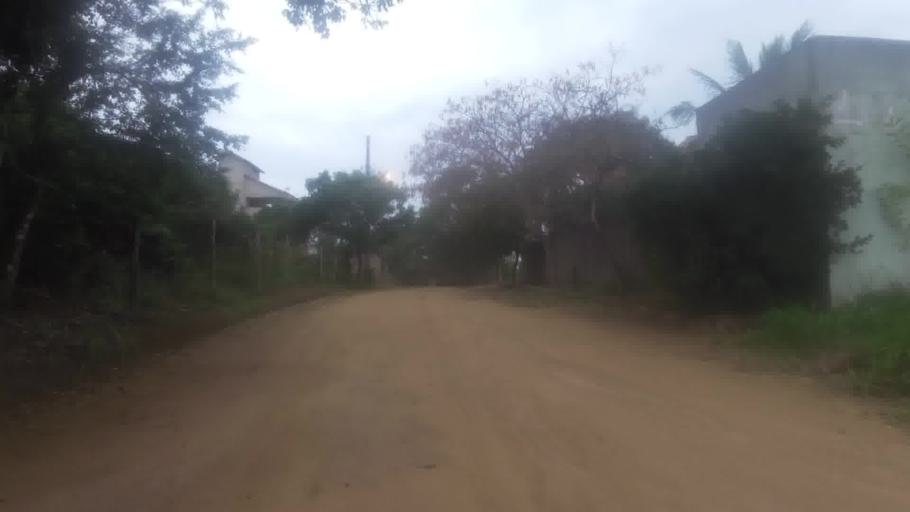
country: BR
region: Espirito Santo
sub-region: Piuma
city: Piuma
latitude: -20.7954
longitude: -40.5877
